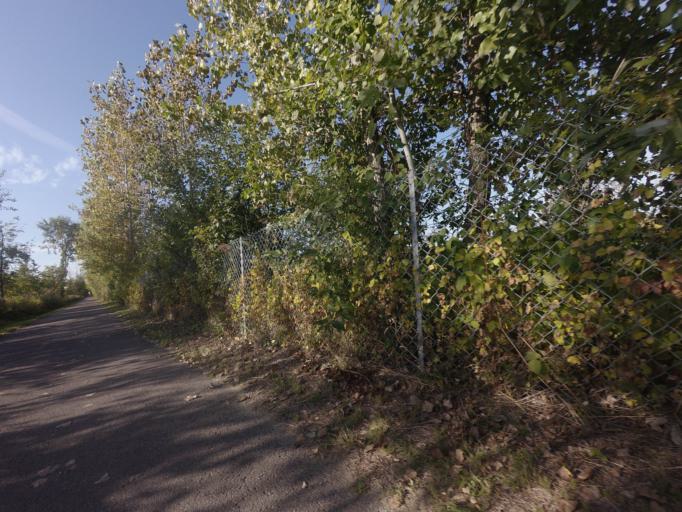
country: CA
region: Quebec
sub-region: Laurentides
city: Blainville
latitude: 45.7253
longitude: -73.9364
